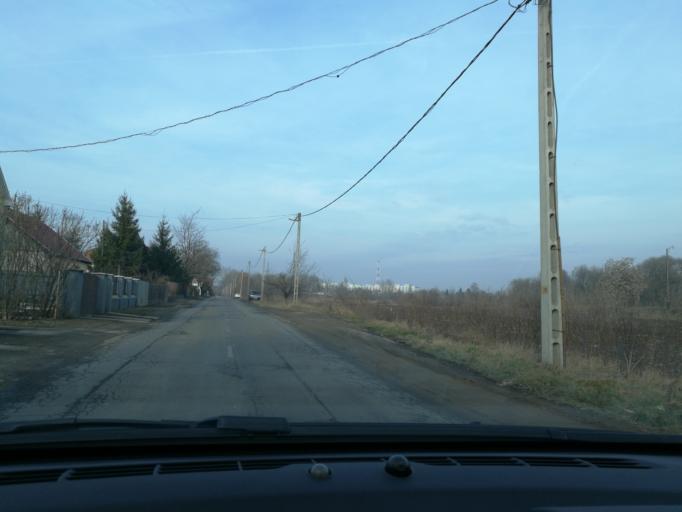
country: HU
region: Szabolcs-Szatmar-Bereg
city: Nyiregyhaza
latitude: 47.9331
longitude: 21.7082
